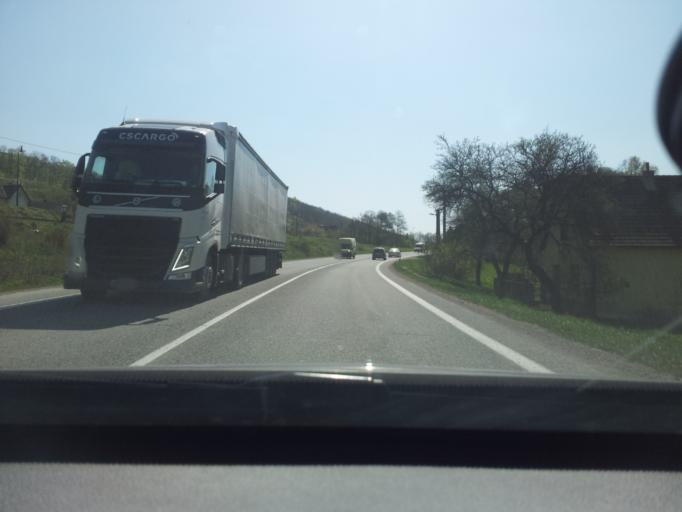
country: SK
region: Trenciansky
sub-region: Okres Trencin
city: Trencin
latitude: 48.8159
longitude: 18.0839
